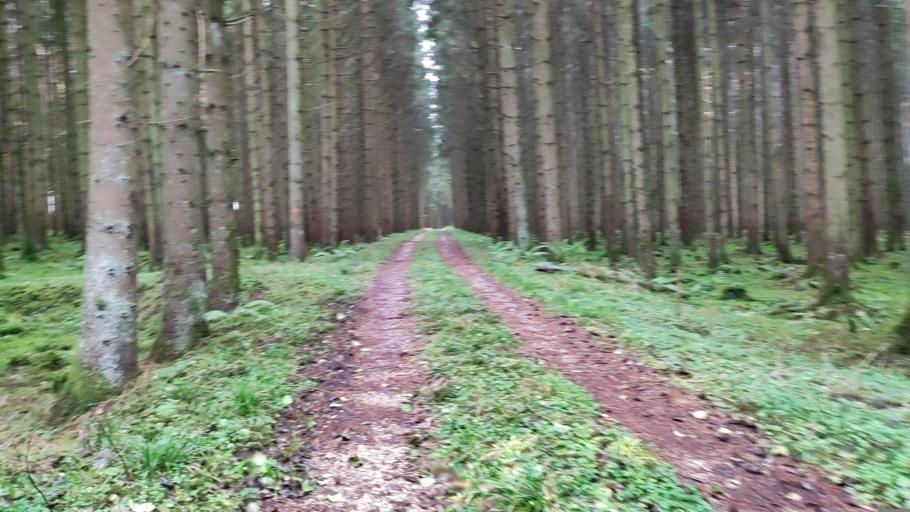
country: DE
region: Bavaria
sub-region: Swabia
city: Landensberg
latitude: 48.3679
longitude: 10.5173
